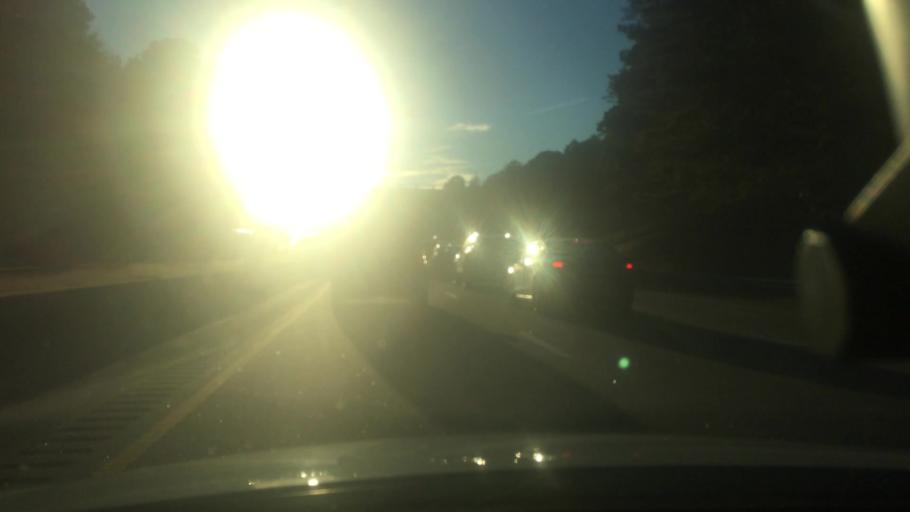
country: US
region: North Carolina
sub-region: Wake County
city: West Raleigh
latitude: 35.8340
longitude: -78.6715
